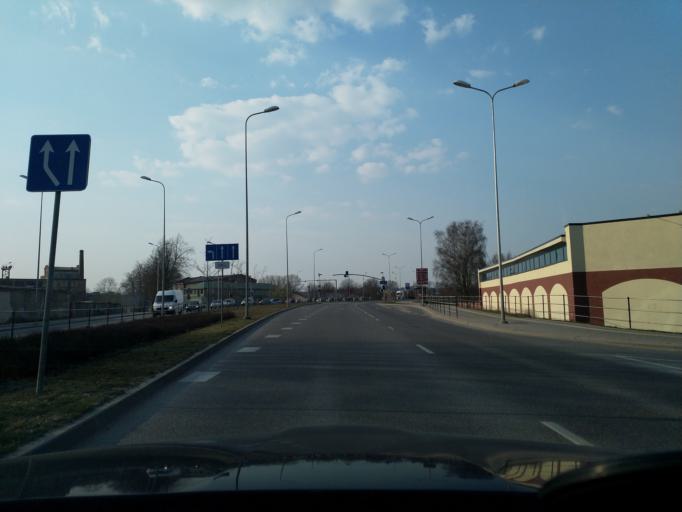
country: LV
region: Liepaja
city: Liepaja
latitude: 56.5105
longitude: 21.0235
